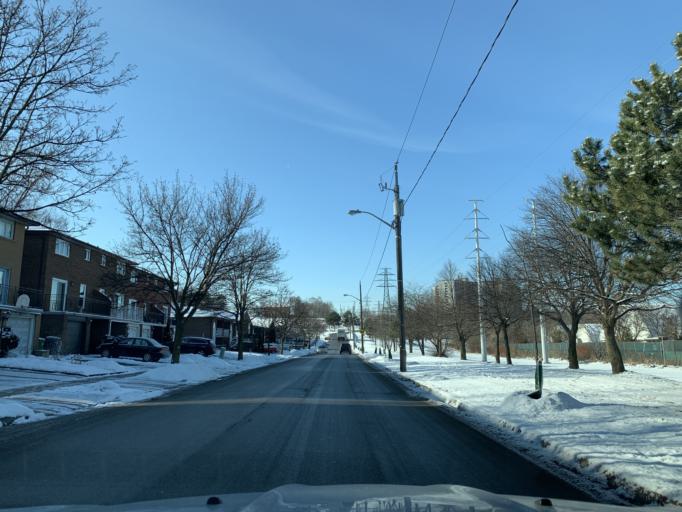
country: CA
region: Ontario
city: Toronto
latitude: 43.6731
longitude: -79.4838
